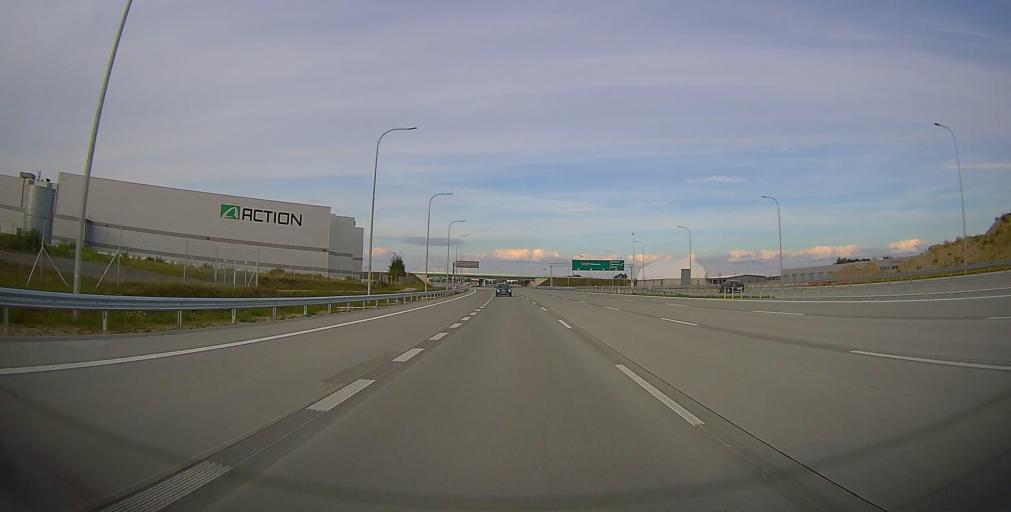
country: PL
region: Masovian Voivodeship
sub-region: Powiat piaseczynski
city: Mysiadlo
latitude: 52.1137
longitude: 20.9823
